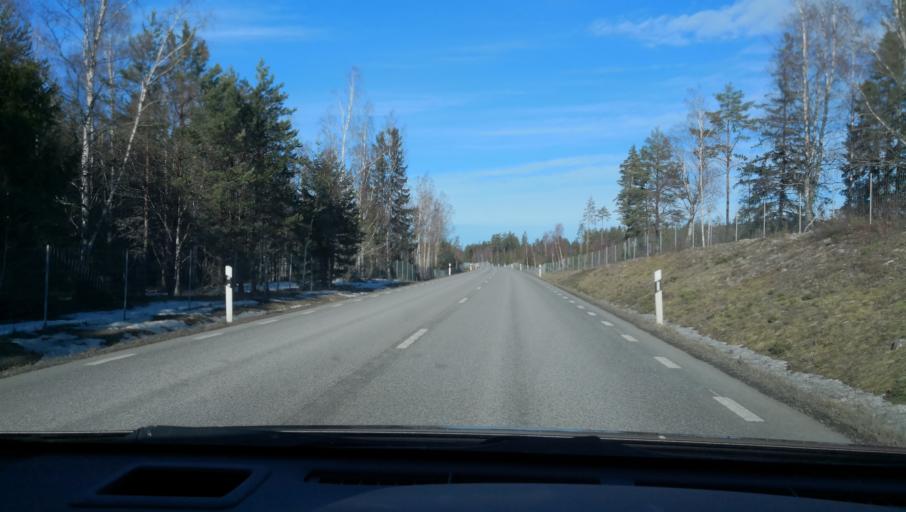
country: SE
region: Uppsala
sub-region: Uppsala Kommun
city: Vattholma
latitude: 60.0394
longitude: 17.7507
